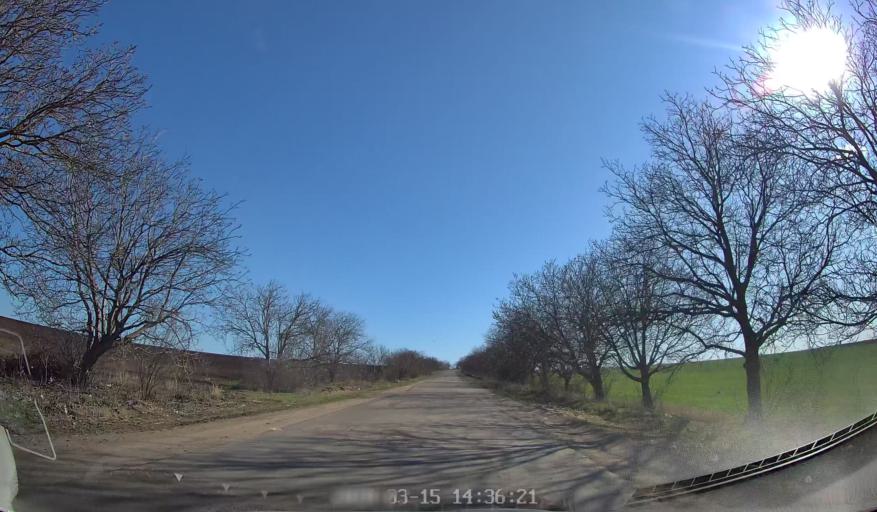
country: MD
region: Orhei
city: Orhei
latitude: 47.3259
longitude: 28.9252
